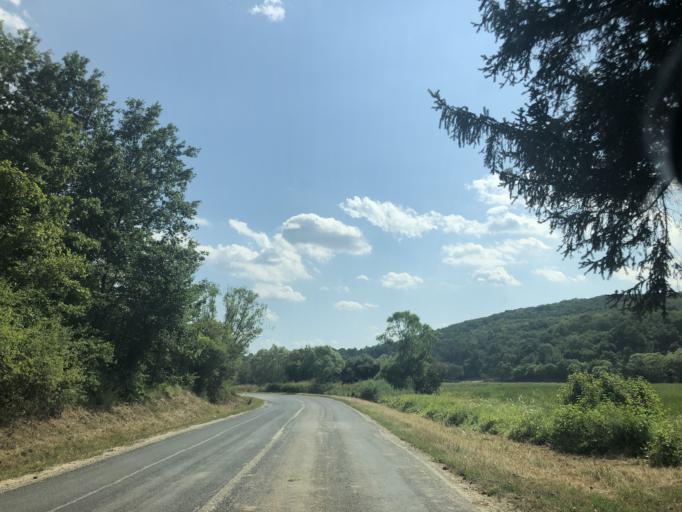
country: HU
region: Borsod-Abauj-Zemplen
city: Szendro
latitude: 48.4468
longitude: 20.7971
